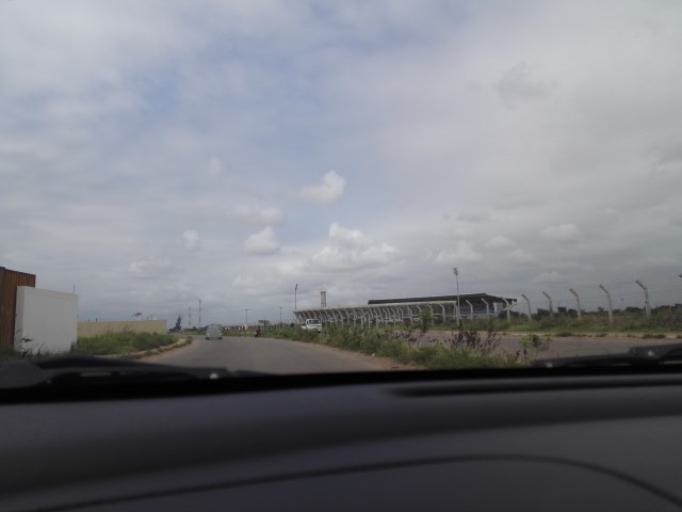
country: MZ
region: Maputo City
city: Maputo
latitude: -25.8242
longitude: 32.5810
